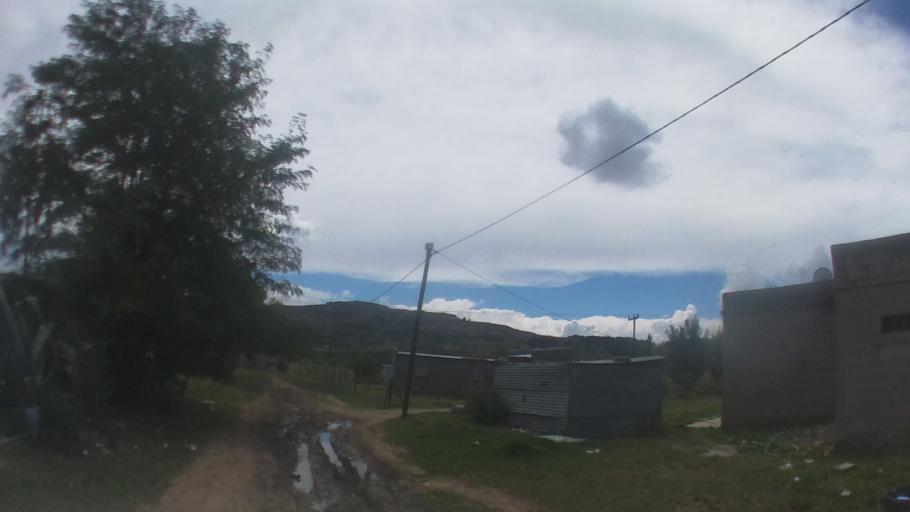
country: LS
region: Maseru
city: Nako
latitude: -29.6186
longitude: 27.5068
